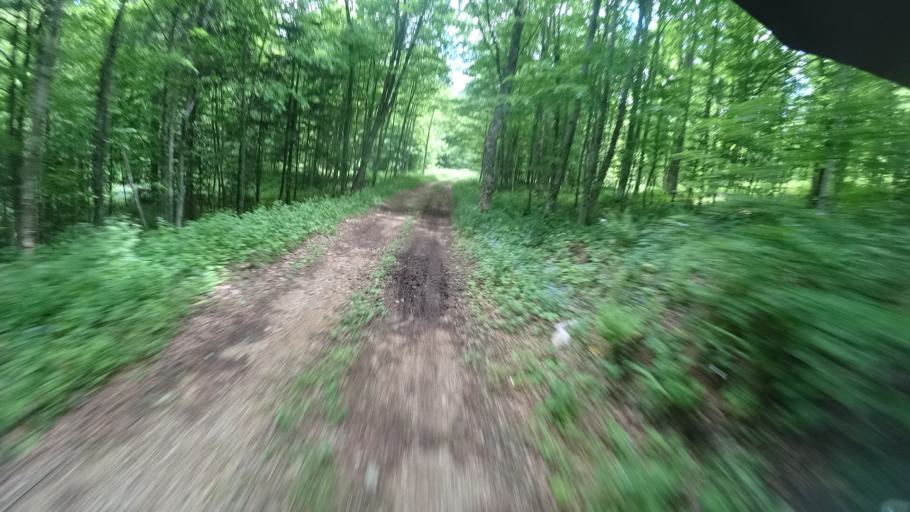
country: HR
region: Zadarska
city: Gracac
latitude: 44.4785
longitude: 15.8837
